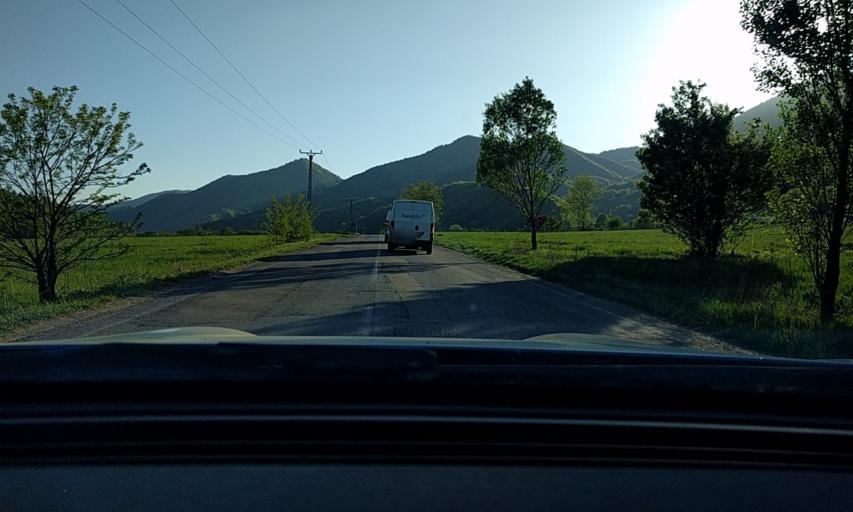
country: RO
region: Bacau
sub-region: Oras Slanic-Moldova
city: Slanic-Moldova
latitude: 46.1832
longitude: 26.4934
